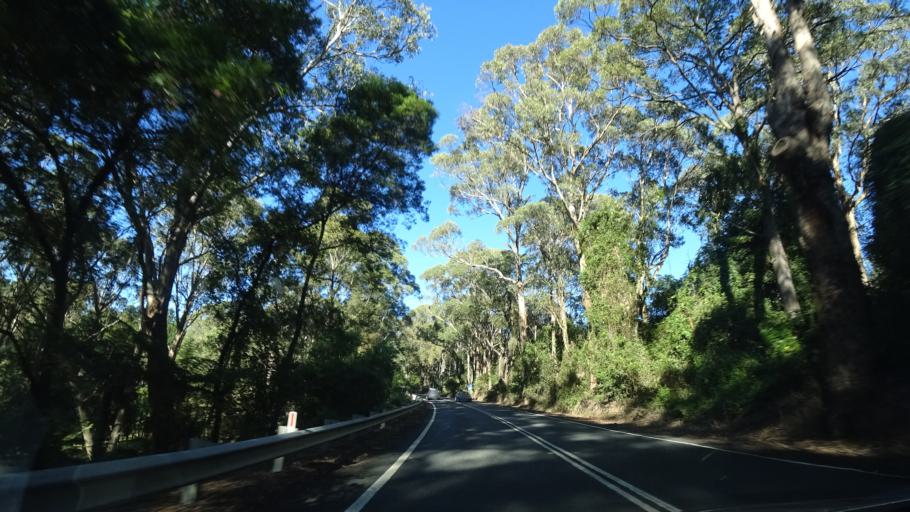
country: AU
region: New South Wales
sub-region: Blue Mountains Municipality
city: Lawson
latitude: -33.5172
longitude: 150.4671
